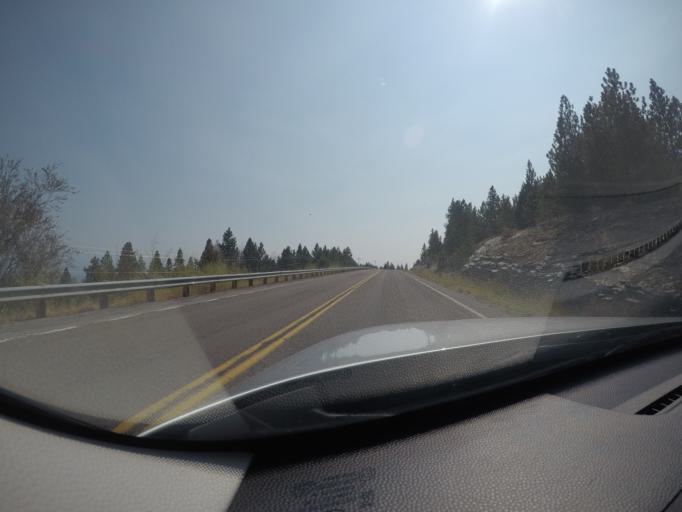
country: US
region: Montana
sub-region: Lake County
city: Polson
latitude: 47.7536
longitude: -114.1686
